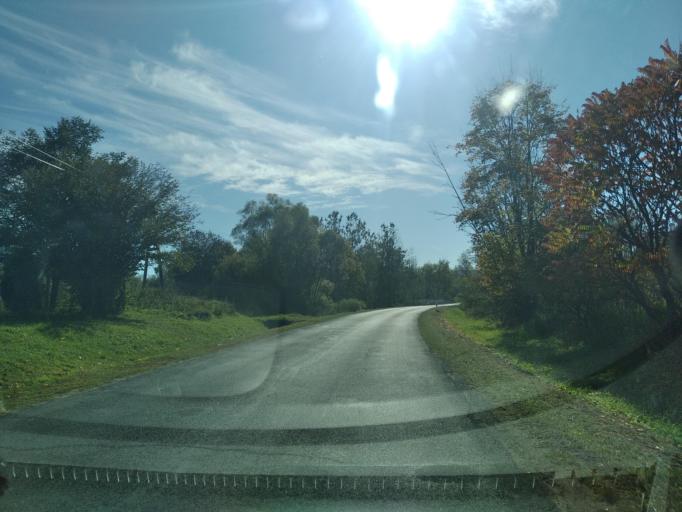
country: PL
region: Subcarpathian Voivodeship
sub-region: Powiat sanocki
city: Komancza
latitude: 49.4096
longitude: 21.9791
